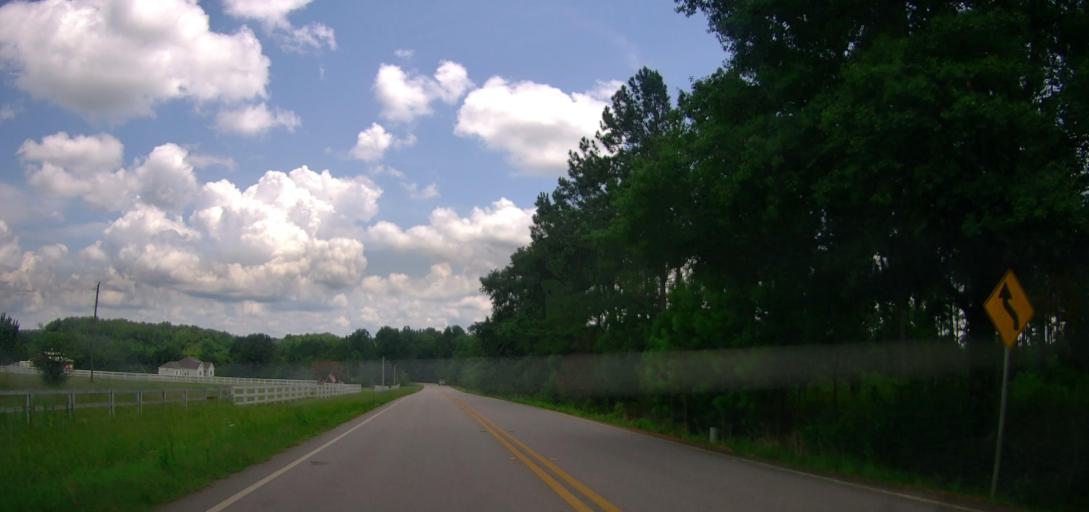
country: US
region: Georgia
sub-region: Meriwether County
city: Greenville
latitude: 33.0610
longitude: -84.7606
